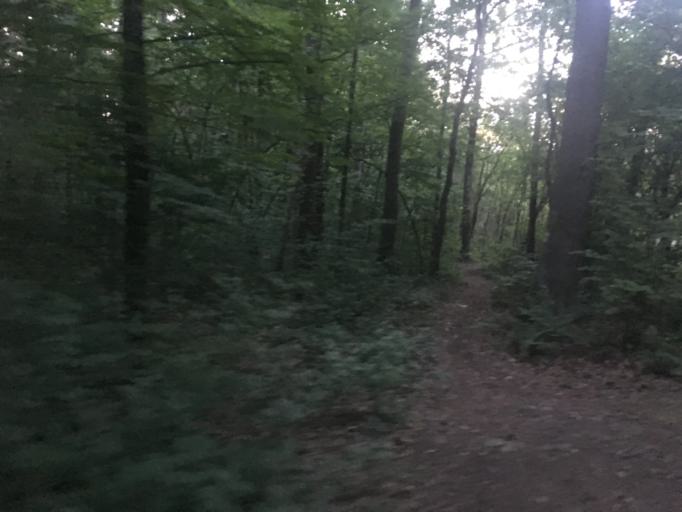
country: BY
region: Grodnenskaya
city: Hrodna
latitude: 53.7152
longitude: 23.7833
